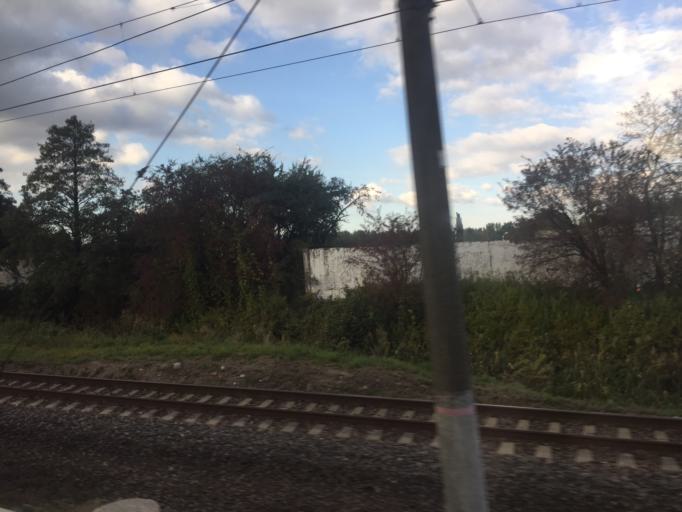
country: RU
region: Kaliningrad
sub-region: Gorod Kaliningrad
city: Kaliningrad
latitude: 54.7671
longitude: 20.4317
